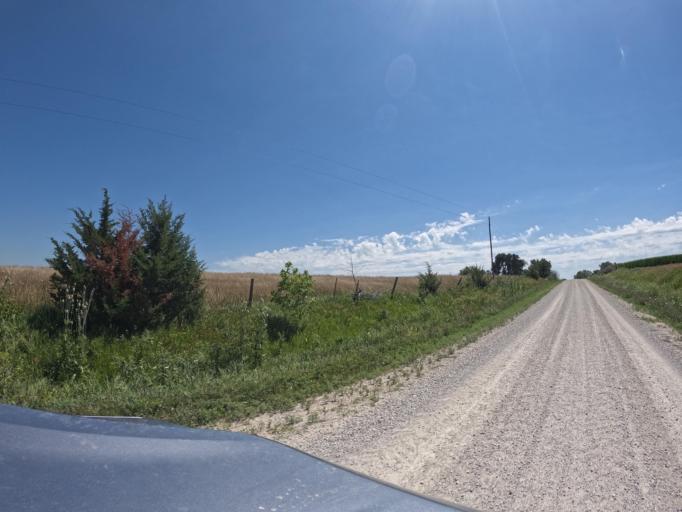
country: US
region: Iowa
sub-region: Keokuk County
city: Sigourney
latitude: 41.4169
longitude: -92.3164
